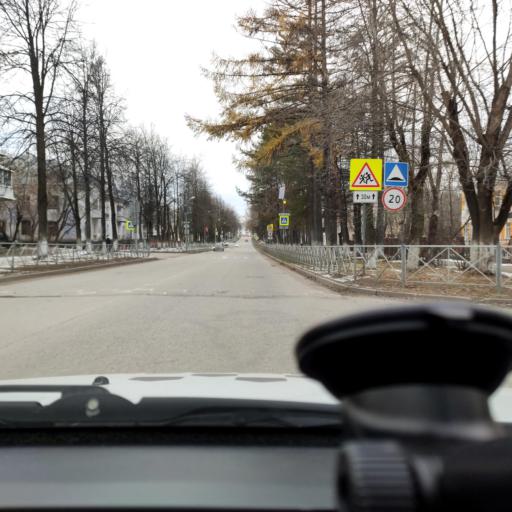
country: RU
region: Perm
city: Perm
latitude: 58.1139
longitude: 56.3169
